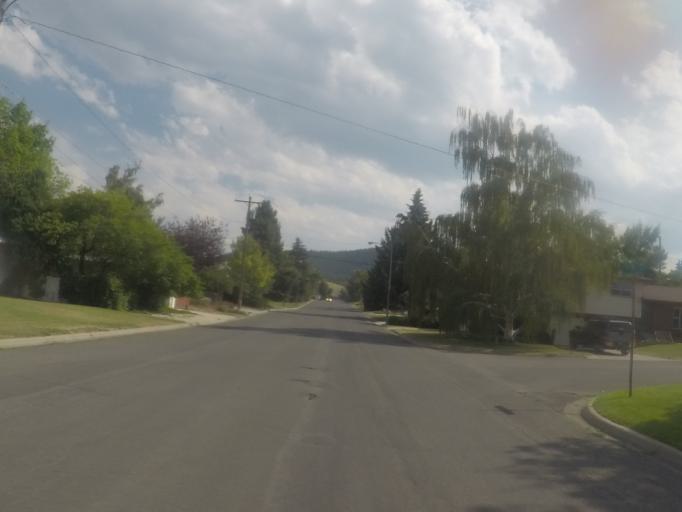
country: US
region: Montana
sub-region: Lewis and Clark County
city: Helena
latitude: 46.5860
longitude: -112.0072
